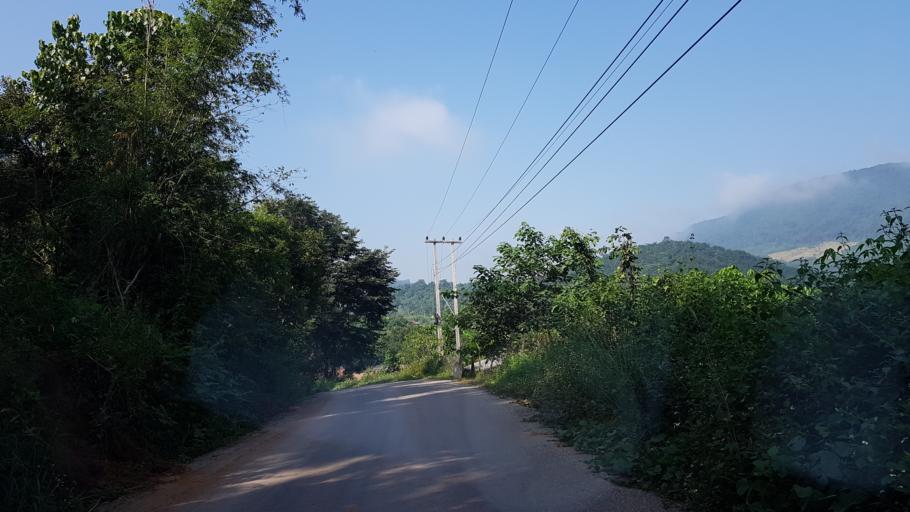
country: LA
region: Oudomxai
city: Muang Xay
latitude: 20.7157
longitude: 102.0926
